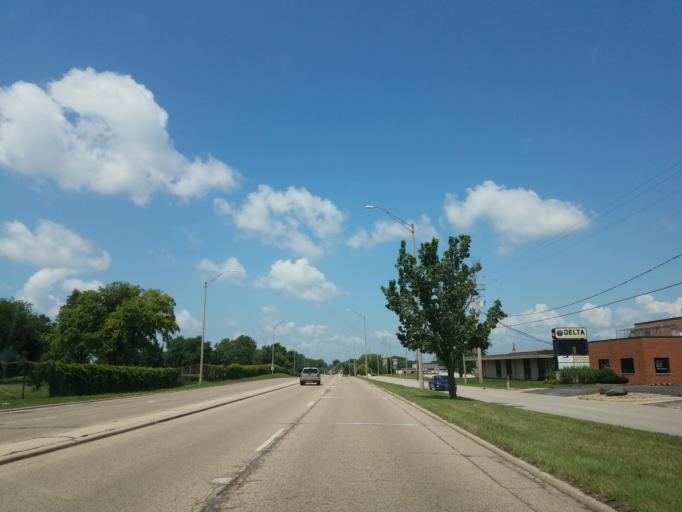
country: US
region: Illinois
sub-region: McLean County
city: Bloomington
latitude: 40.4885
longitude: -88.9637
